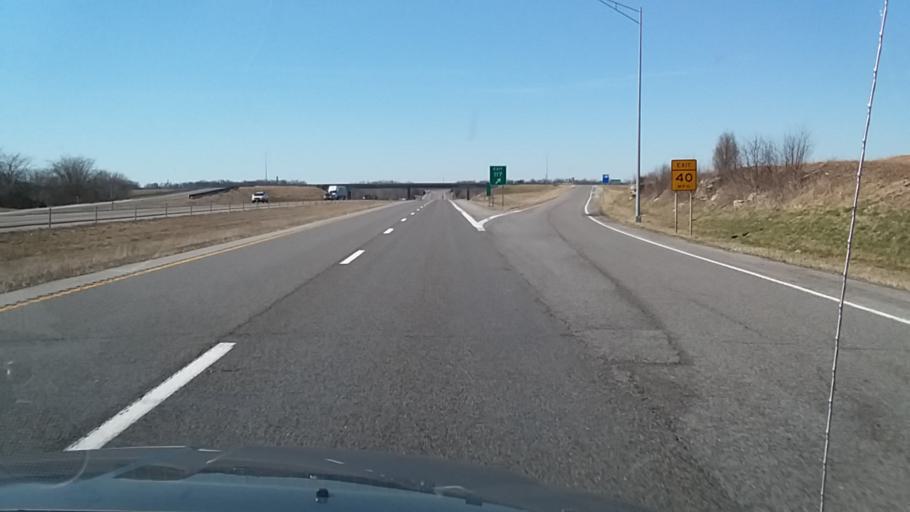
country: US
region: Missouri
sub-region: Perry County
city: Perryville
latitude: 37.5745
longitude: -89.7567
